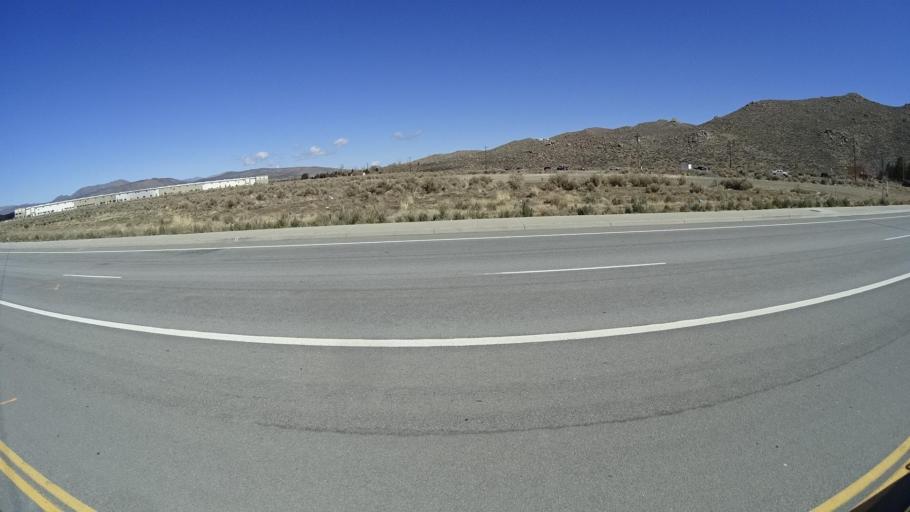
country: US
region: Nevada
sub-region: Washoe County
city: Lemmon Valley
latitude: 39.6241
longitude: -119.8495
